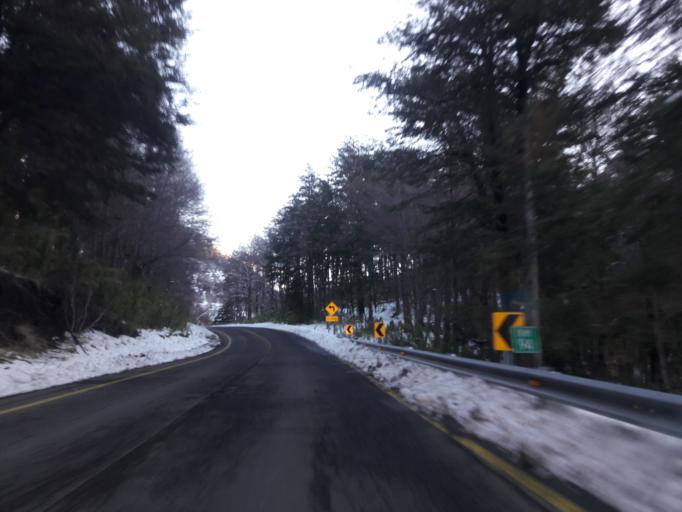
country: CL
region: Araucania
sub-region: Provincia de Cautin
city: Vilcun
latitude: -38.5040
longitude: -71.5204
